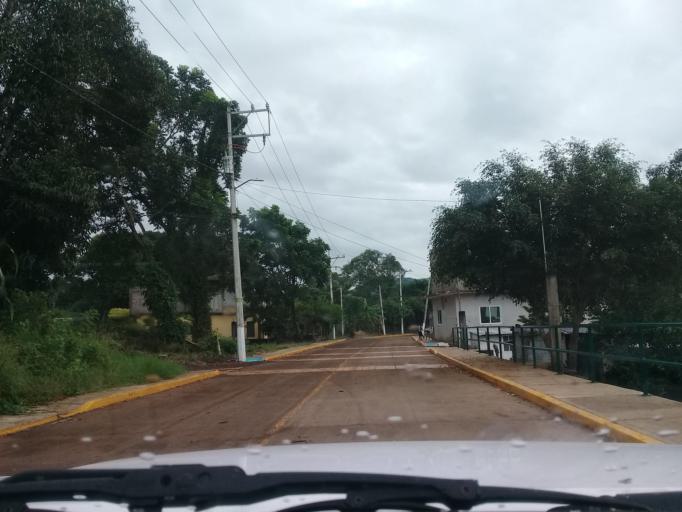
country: MX
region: Veracruz
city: San Andres Tuxtla
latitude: 18.4344
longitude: -95.2099
